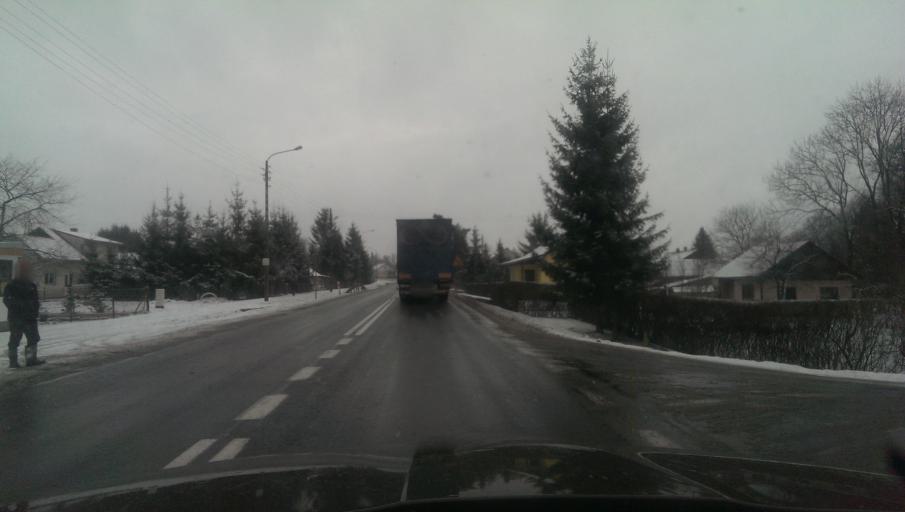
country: PL
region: Subcarpathian Voivodeship
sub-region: Powiat sanocki
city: Nowosielce-Gniewosz
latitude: 49.5675
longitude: 22.0708
